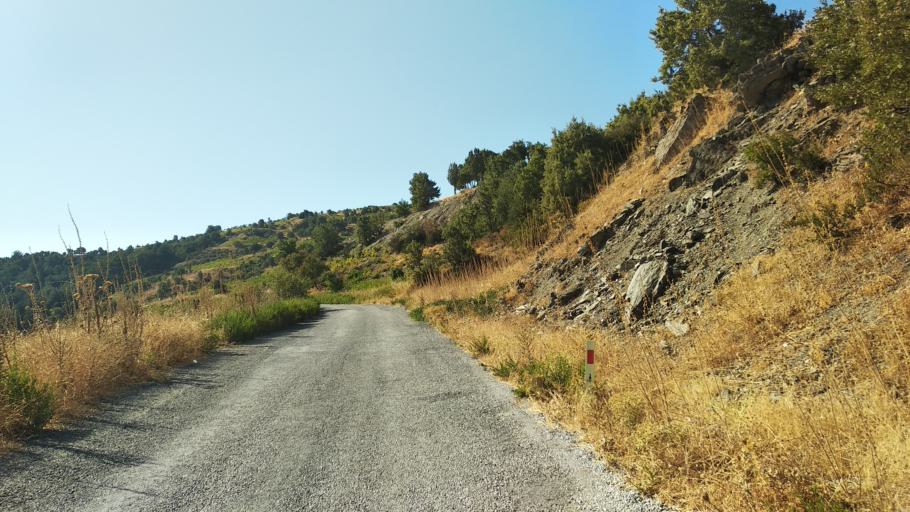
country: TR
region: Izmir
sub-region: Seferihisar
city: Seferhisar
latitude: 38.3283
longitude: 26.9499
